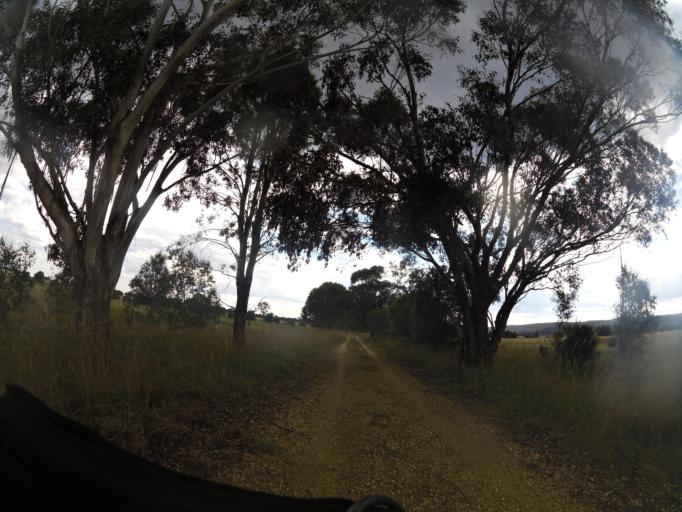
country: AU
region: Victoria
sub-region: Wellington
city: Heyfield
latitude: -38.0190
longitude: 146.6834
